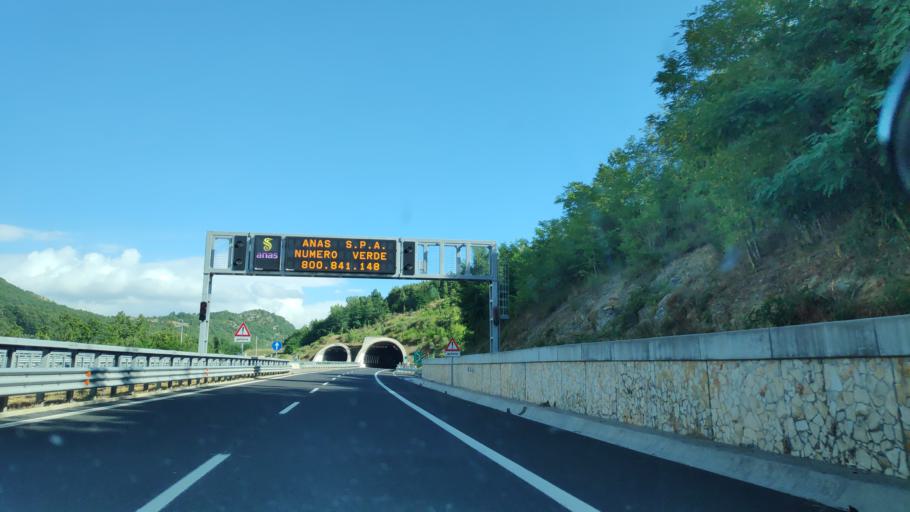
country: IT
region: Campania
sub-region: Provincia di Salerno
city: Casalbuono
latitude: 40.2295
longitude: 15.6684
